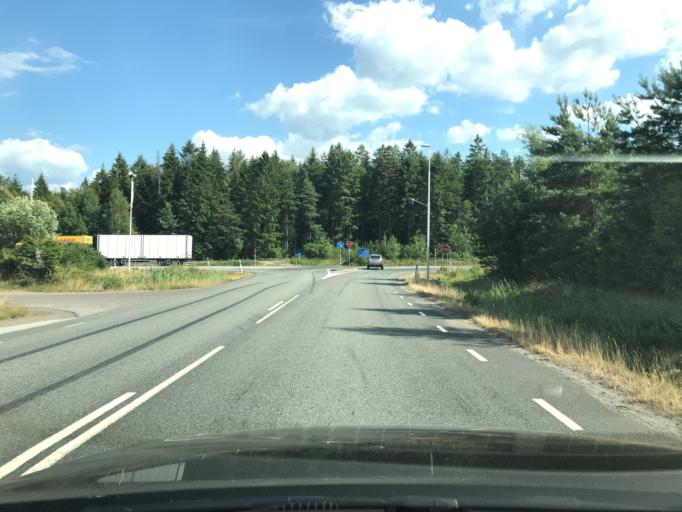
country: SE
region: Skane
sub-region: Hassleholms Kommun
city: Hastveda
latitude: 56.2723
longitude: 13.9533
